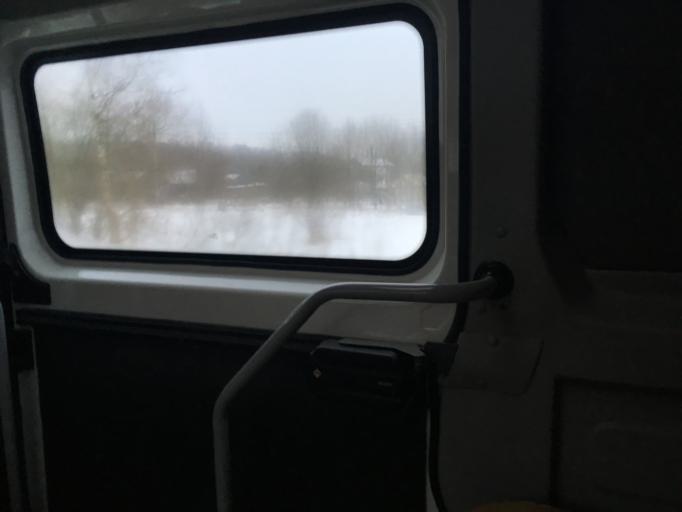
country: RU
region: Tula
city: Krapivna
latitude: 54.1372
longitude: 37.2809
